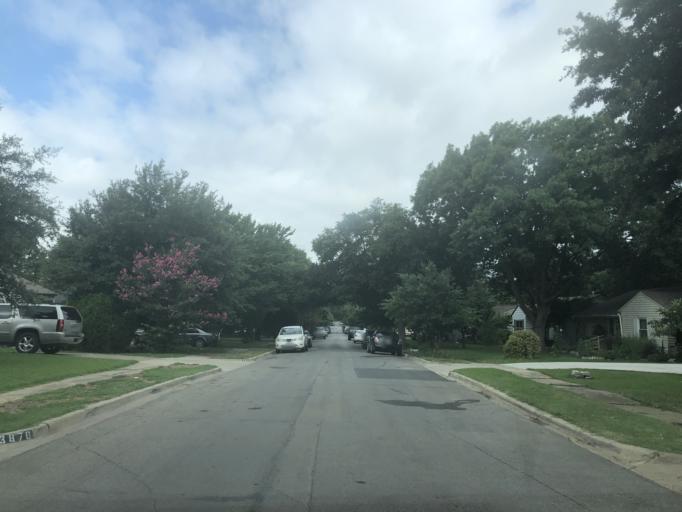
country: US
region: Texas
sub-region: Dallas County
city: University Park
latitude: 32.8681
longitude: -96.8500
